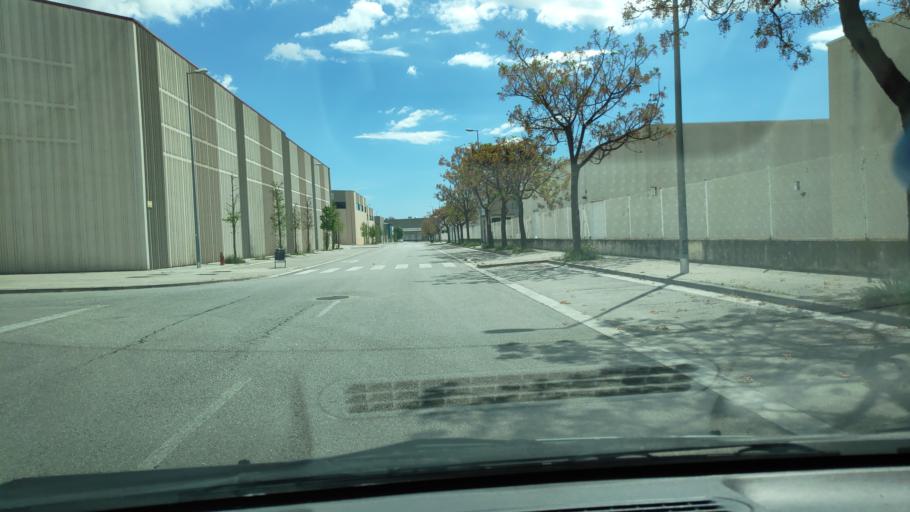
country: ES
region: Catalonia
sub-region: Provincia de Barcelona
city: Polinya
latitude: 41.5411
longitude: 2.1359
